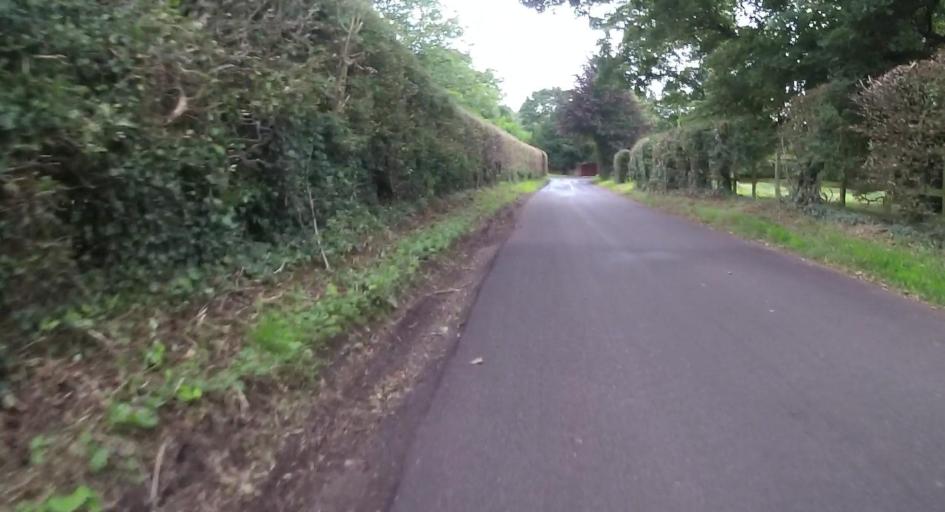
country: GB
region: England
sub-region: Hampshire
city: Andover
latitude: 51.1937
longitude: -1.3947
